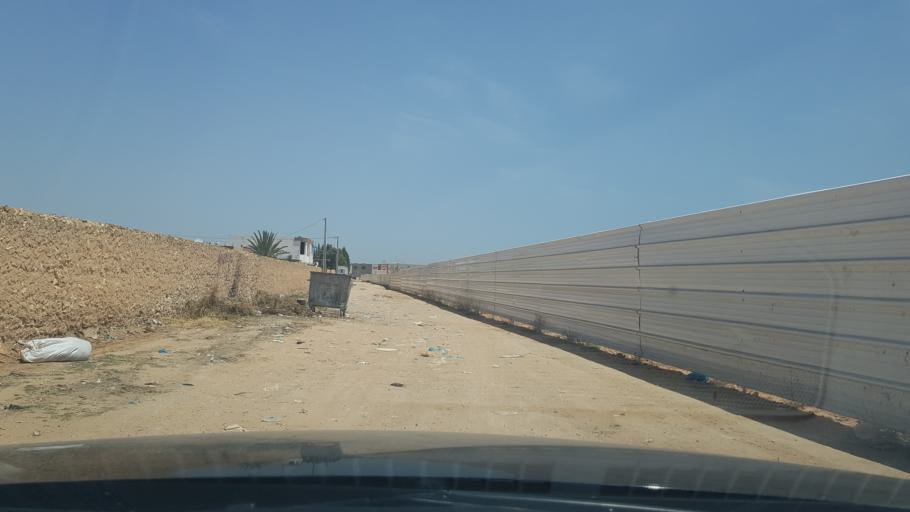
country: TN
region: Safaqis
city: Al Qarmadah
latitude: 34.8416
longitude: 10.7592
